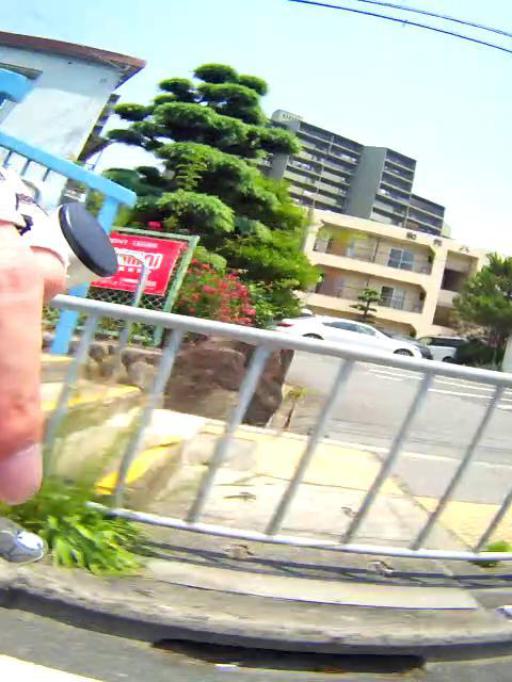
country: JP
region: Osaka
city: Toyonaka
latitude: 34.8012
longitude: 135.4939
